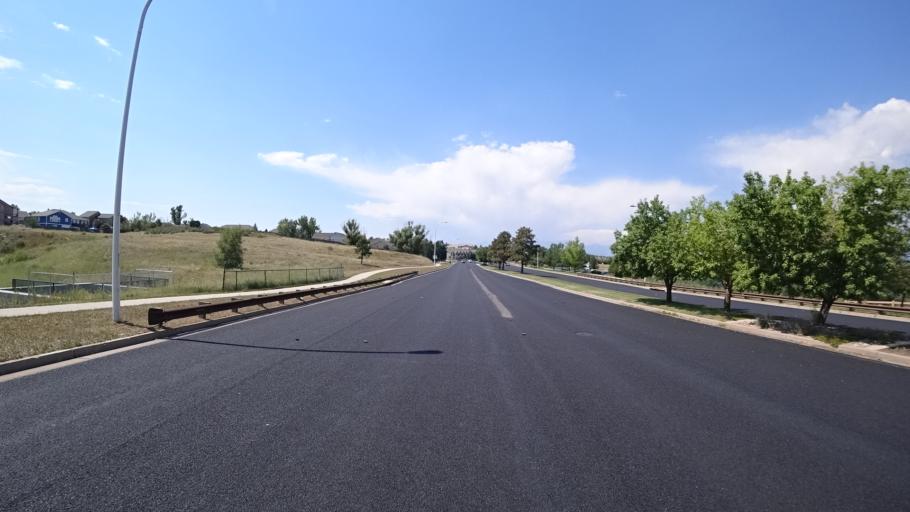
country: US
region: Colorado
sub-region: El Paso County
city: Cimarron Hills
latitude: 38.9294
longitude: -104.7486
